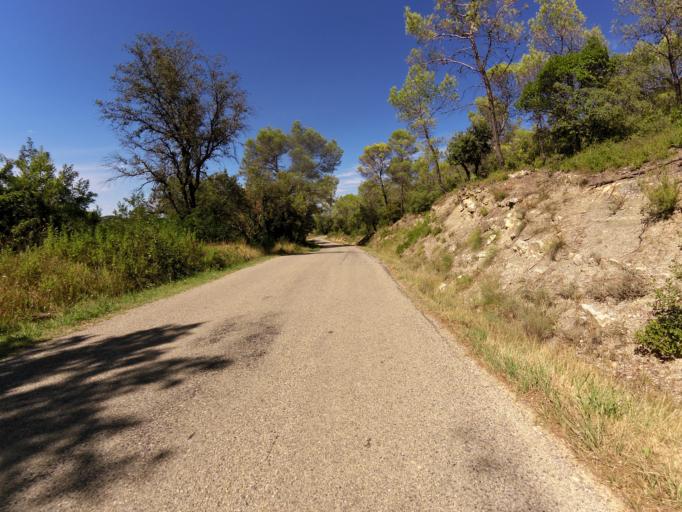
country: FR
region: Languedoc-Roussillon
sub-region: Departement du Gard
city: Quissac
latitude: 43.9130
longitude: 4.0486
